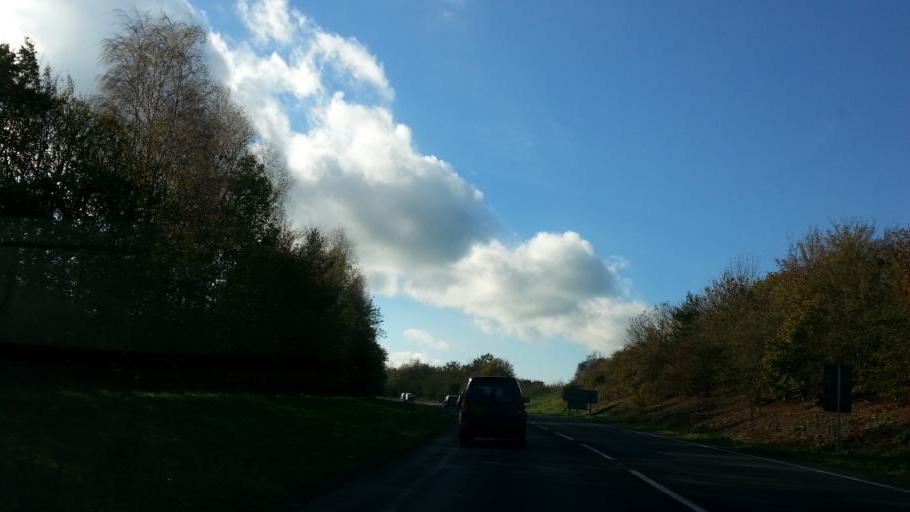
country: GB
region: England
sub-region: Norfolk
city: Harleston
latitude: 52.3933
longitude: 1.2804
